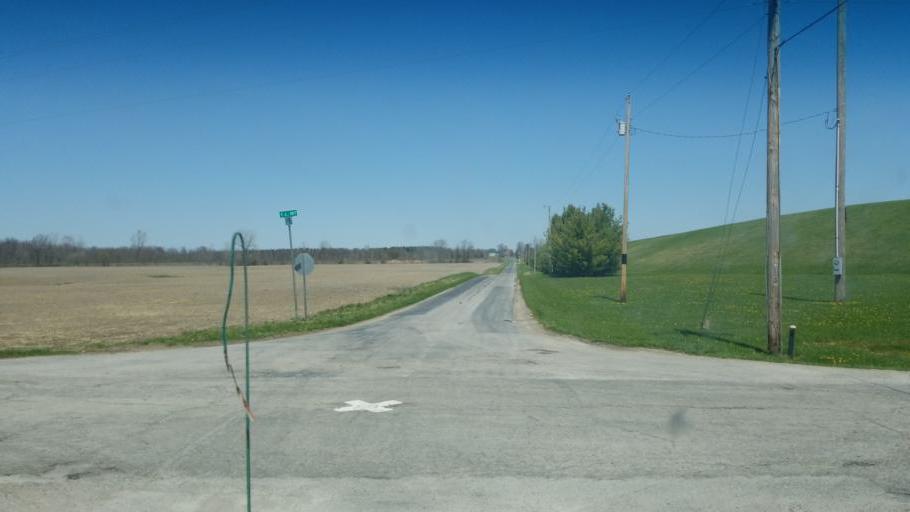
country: US
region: Ohio
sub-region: Huron County
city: New London
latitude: 41.0653
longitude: -82.4369
